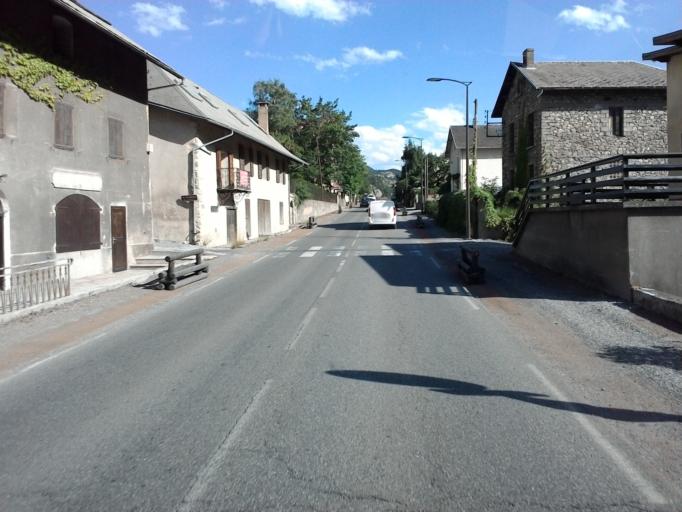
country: FR
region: Provence-Alpes-Cote d'Azur
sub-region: Departement des Hautes-Alpes
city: Saint-Martin-de-Queyrieres
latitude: 44.7516
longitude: 6.5775
